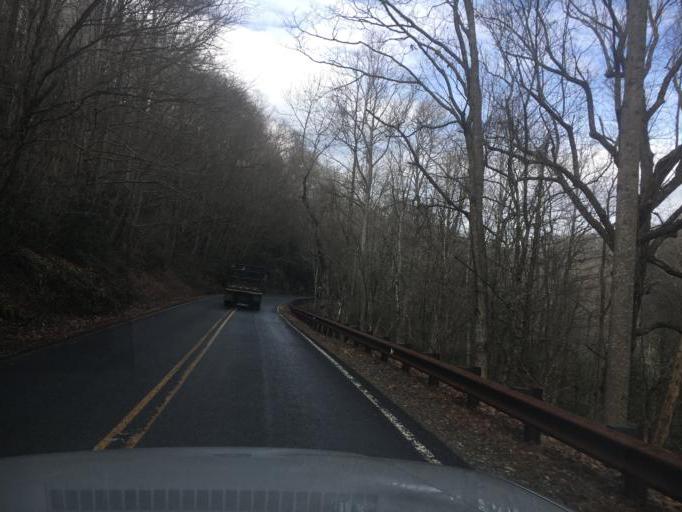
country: US
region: North Carolina
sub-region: Haywood County
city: Canton
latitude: 35.3796
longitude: -82.8098
